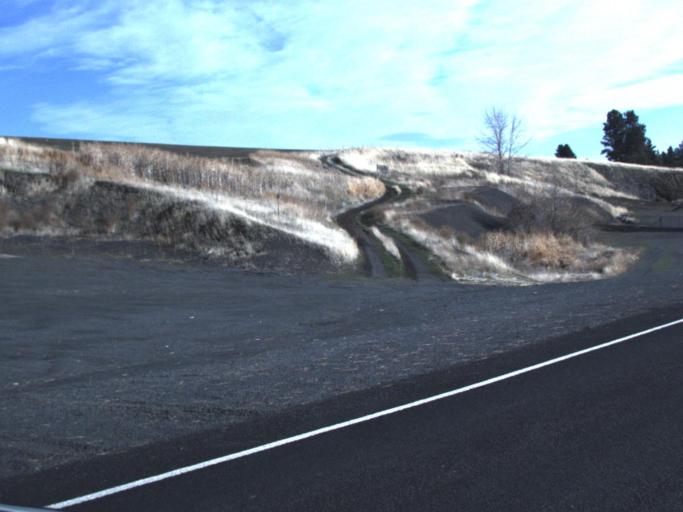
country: US
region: Washington
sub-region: Whitman County
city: Pullman
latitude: 46.9293
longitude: -117.1148
